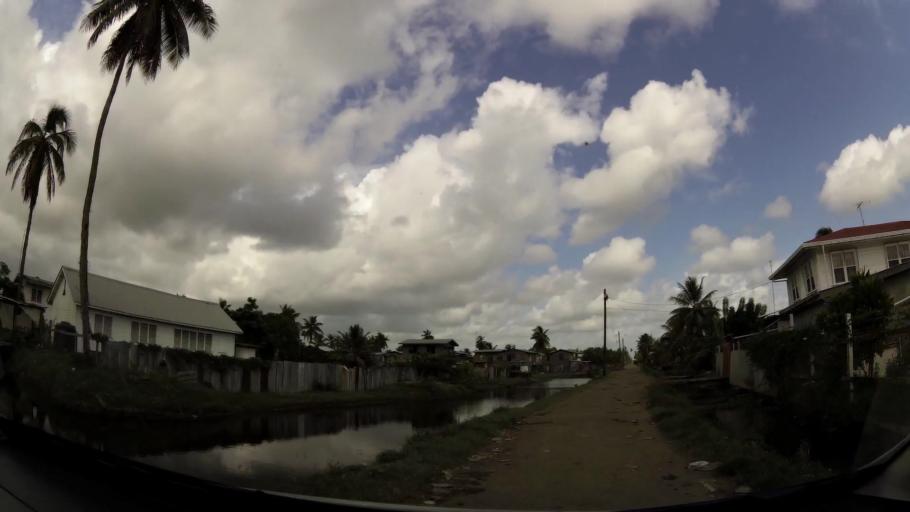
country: GY
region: Demerara-Mahaica
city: Mahaica Village
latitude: 6.6672
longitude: -57.9257
